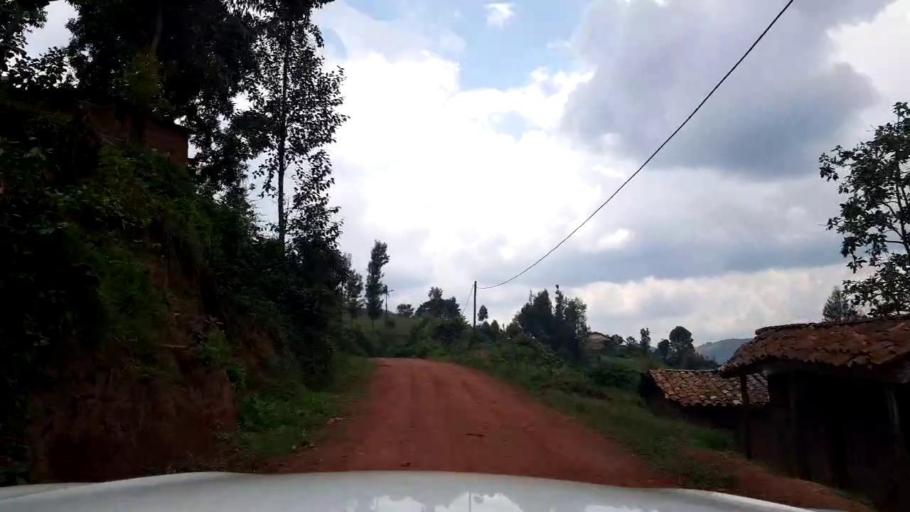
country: RW
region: Northern Province
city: Byumba
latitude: -1.4828
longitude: 29.9057
